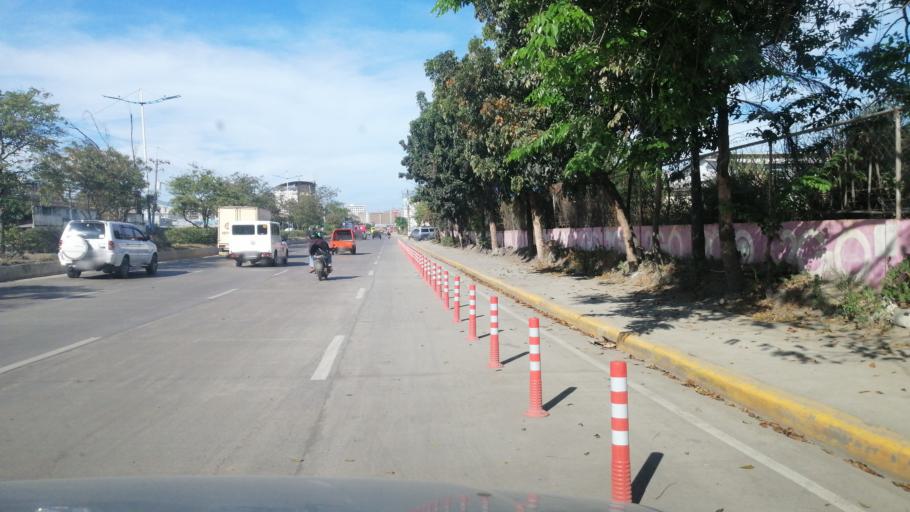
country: PH
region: Central Visayas
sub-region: Cebu City
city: Baugo
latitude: 10.3133
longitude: 123.9248
